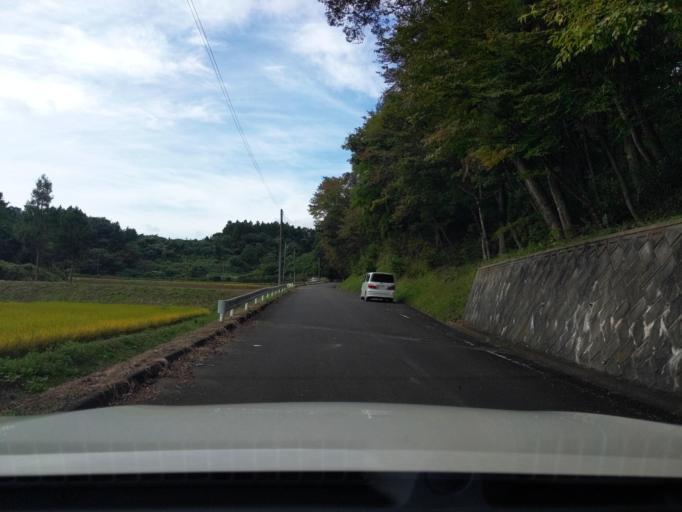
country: JP
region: Fukushima
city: Koriyama
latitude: 37.4114
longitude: 140.2786
